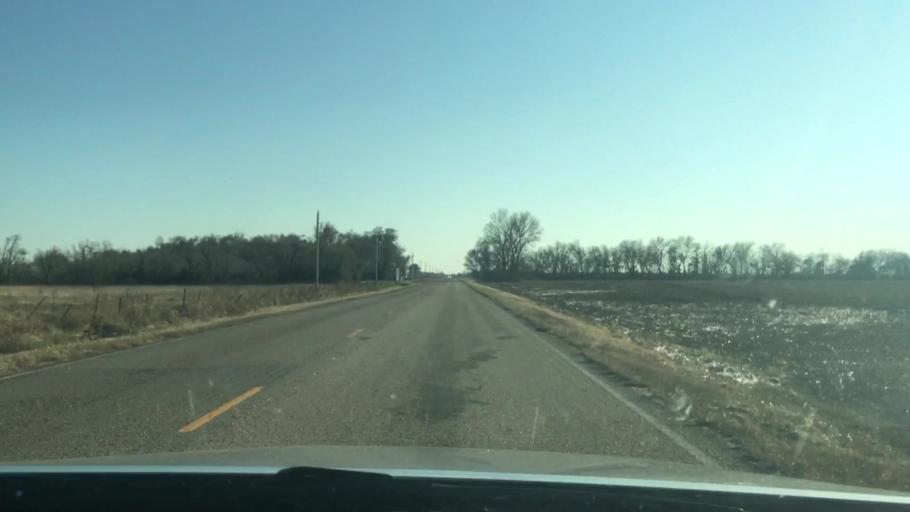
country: US
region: Kansas
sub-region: Reno County
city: Nickerson
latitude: 38.1842
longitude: -98.0876
